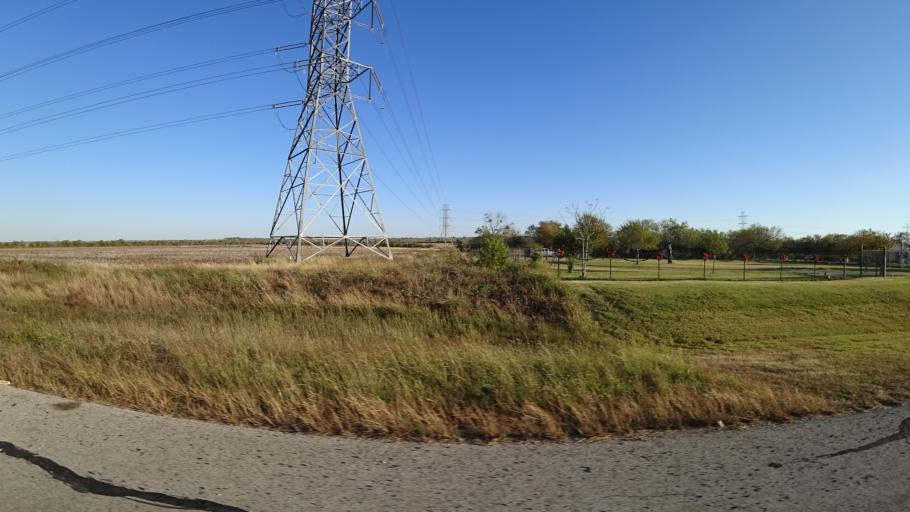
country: US
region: Texas
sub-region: Travis County
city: Onion Creek
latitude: 30.0846
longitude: -97.6862
